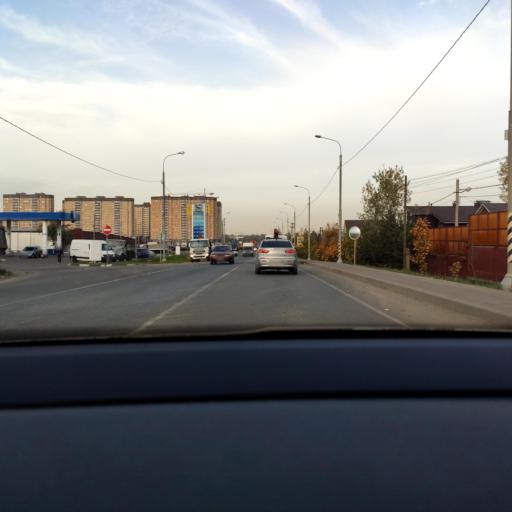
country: RU
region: Moskovskaya
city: Pirogovskiy
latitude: 55.9705
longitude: 37.7492
